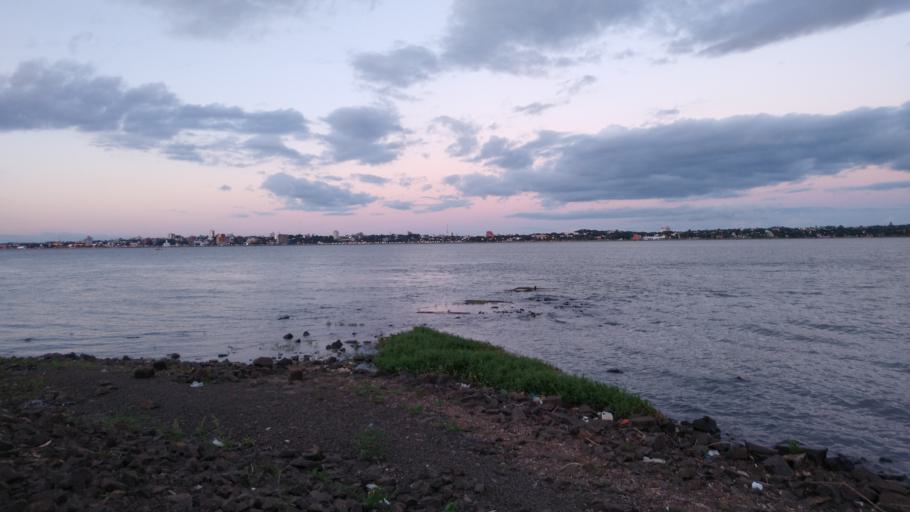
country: AR
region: Misiones
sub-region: Departamento de Capital
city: Posadas
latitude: -27.3615
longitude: -55.8852
